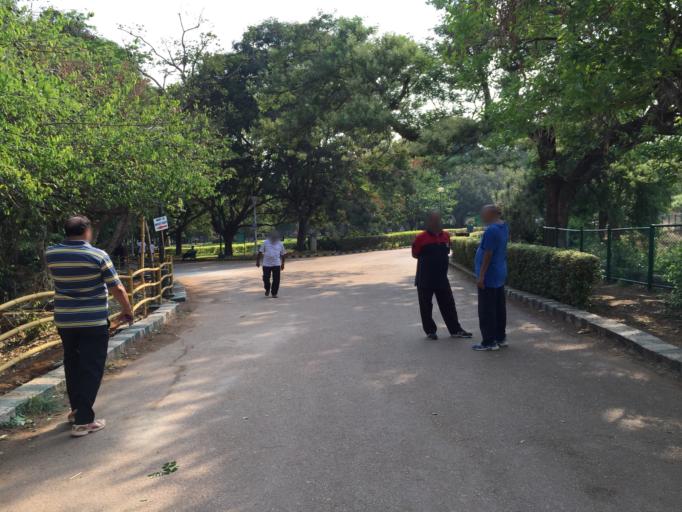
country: IN
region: Karnataka
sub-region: Bangalore Urban
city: Bangalore
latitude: 12.9477
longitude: 77.5857
